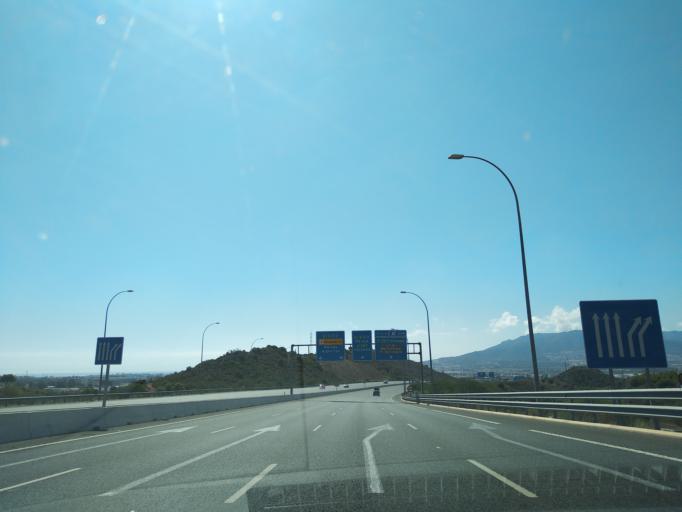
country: ES
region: Andalusia
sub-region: Provincia de Malaga
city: Alhaurin de la Torre
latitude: 36.7318
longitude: -4.5070
